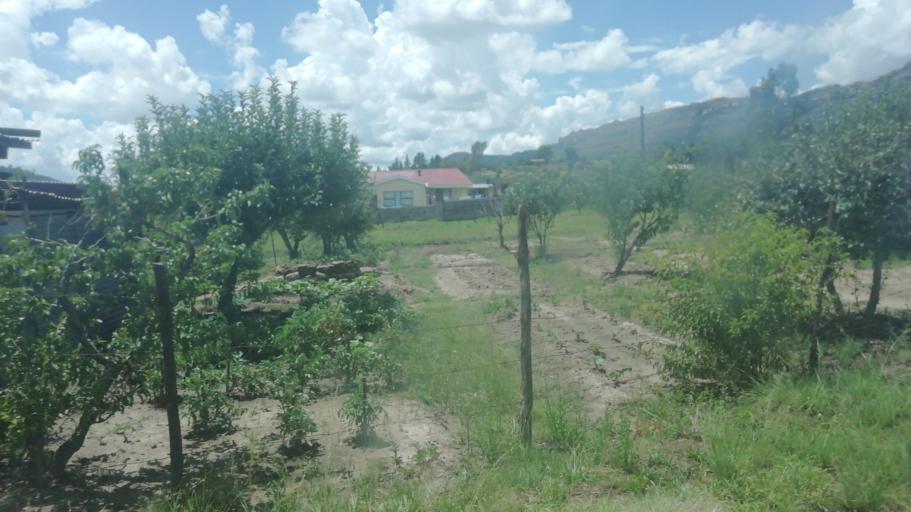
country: LS
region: Maseru
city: Nako
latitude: -29.6186
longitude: 27.5179
